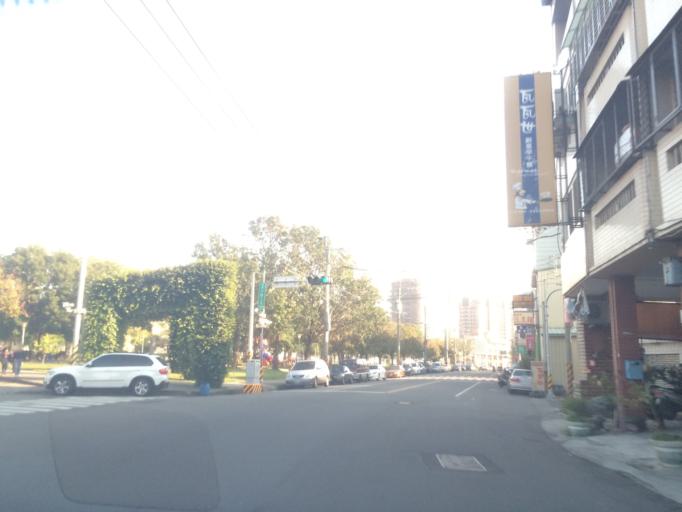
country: TW
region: Taiwan
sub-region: Taichung City
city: Taichung
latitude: 24.1905
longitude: 120.6849
